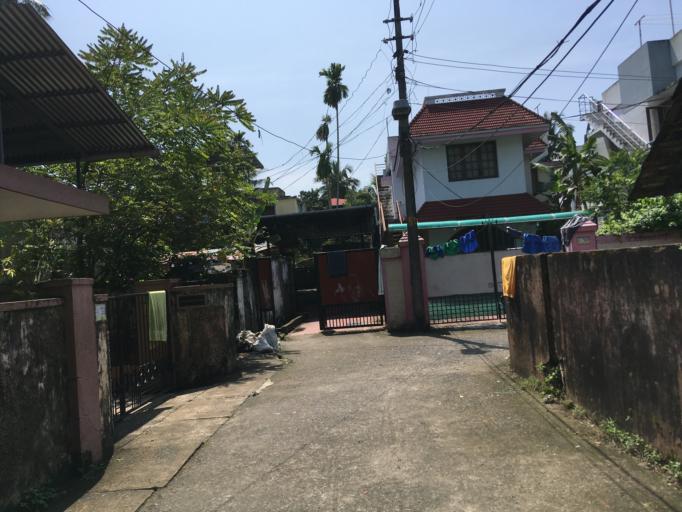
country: IN
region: Kerala
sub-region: Ernakulam
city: Cochin
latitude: 9.9587
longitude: 76.2446
